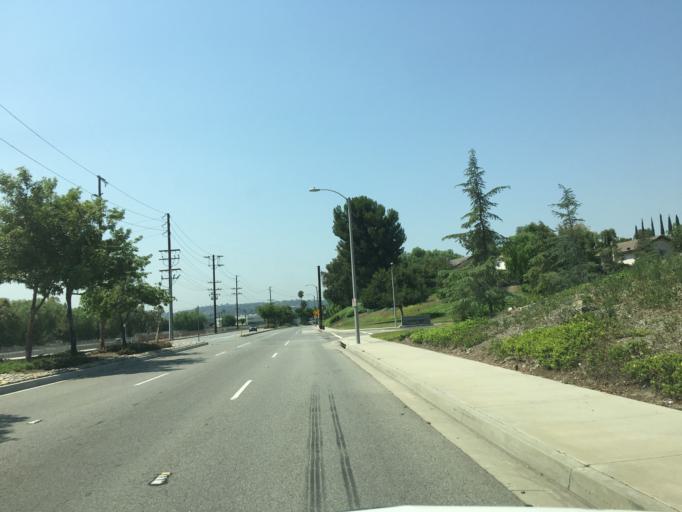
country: US
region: California
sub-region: Los Angeles County
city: Walnut
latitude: 34.0239
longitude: -117.8378
